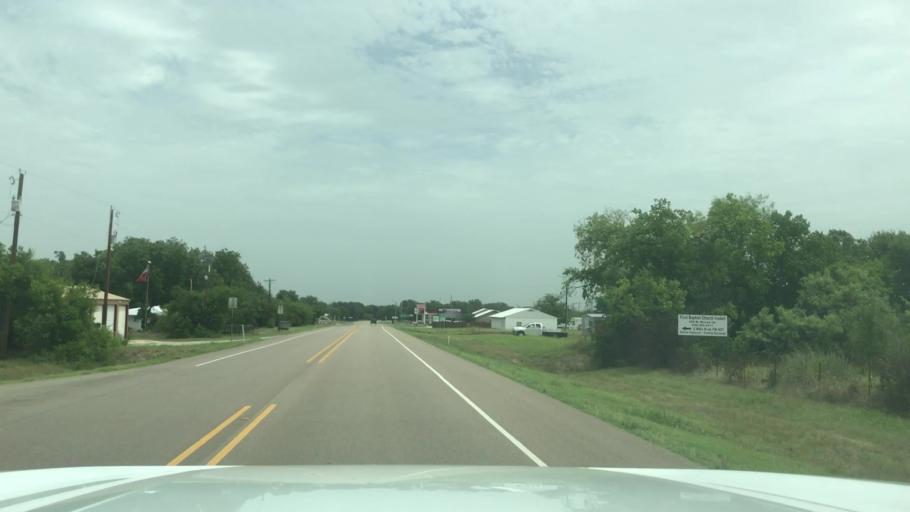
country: US
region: Texas
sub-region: Hamilton County
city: Hico
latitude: 31.9799
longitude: -97.8736
